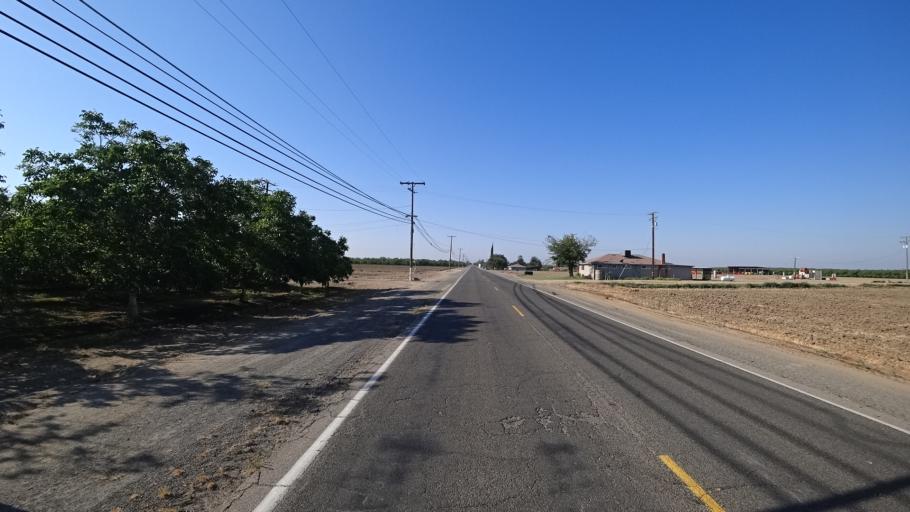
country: US
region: California
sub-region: Kings County
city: Lucerne
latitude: 36.3685
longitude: -119.7090
